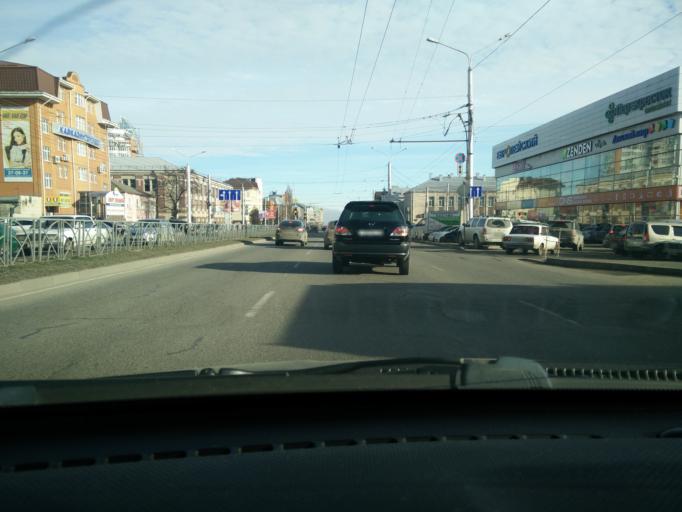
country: RU
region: Stavropol'skiy
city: Stavropol'
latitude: 45.0345
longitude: 41.9653
